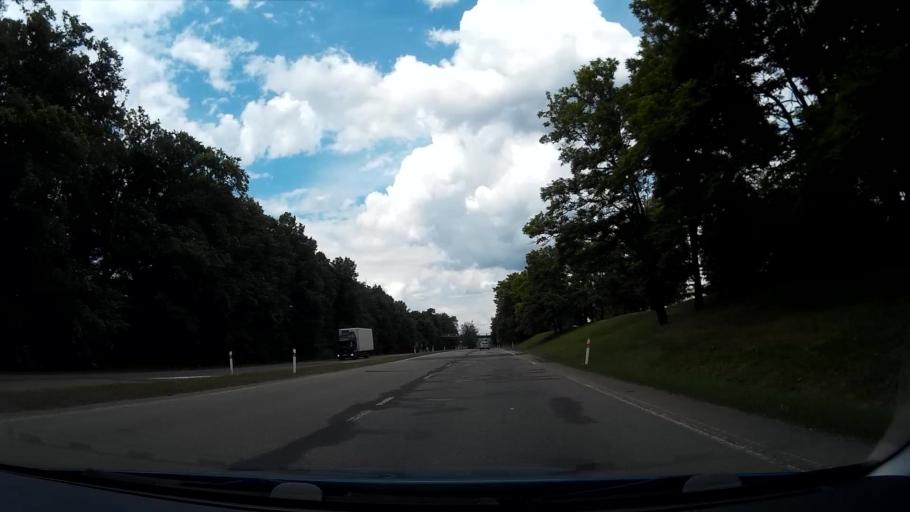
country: CZ
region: South Moravian
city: Troubsko
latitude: 49.2182
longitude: 16.5215
